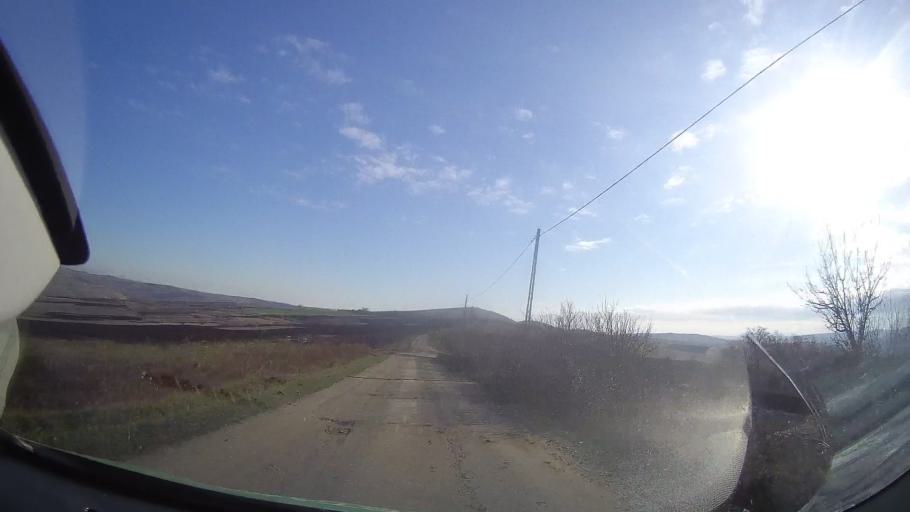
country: RO
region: Mures
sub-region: Comuna Papiu Ilarian
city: Papiu Ilarian
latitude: 46.5856
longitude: 24.2262
